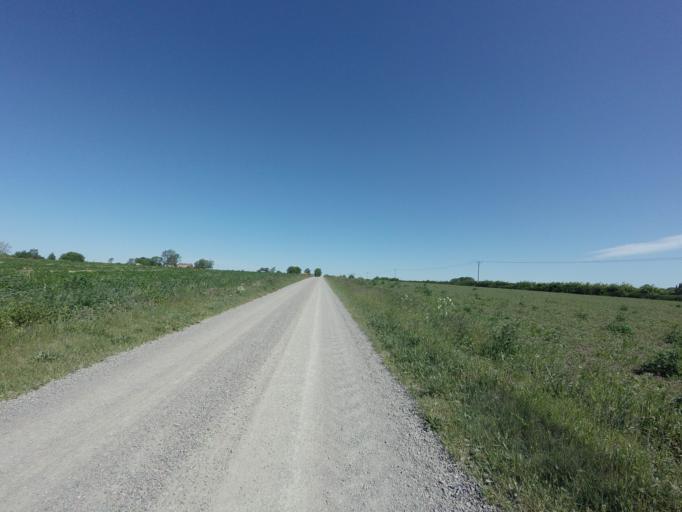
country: SE
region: Skane
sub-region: Helsingborg
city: Odakra
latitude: 56.1014
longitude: 12.7169
